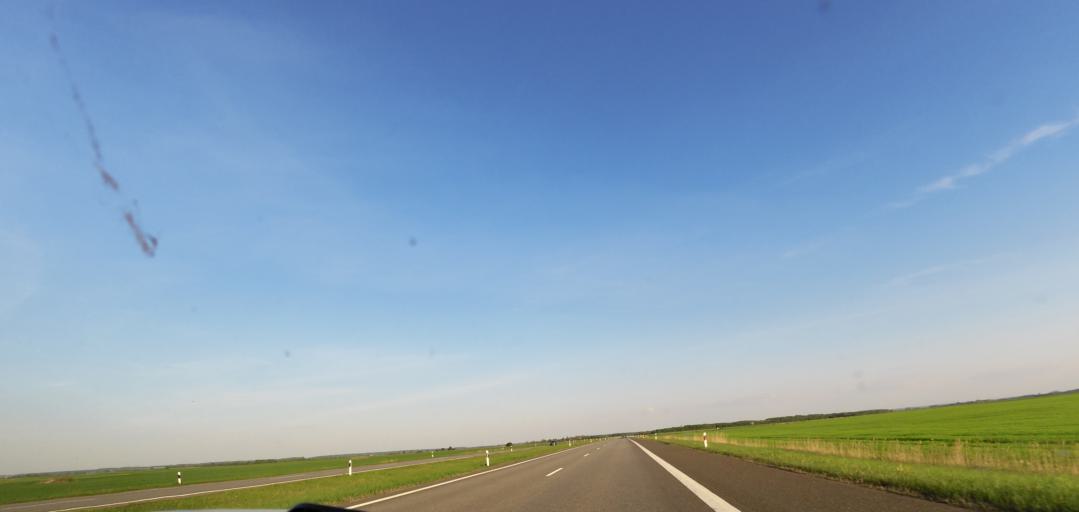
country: LT
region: Vilnius County
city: Ukmerge
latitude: 55.3735
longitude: 24.7215
